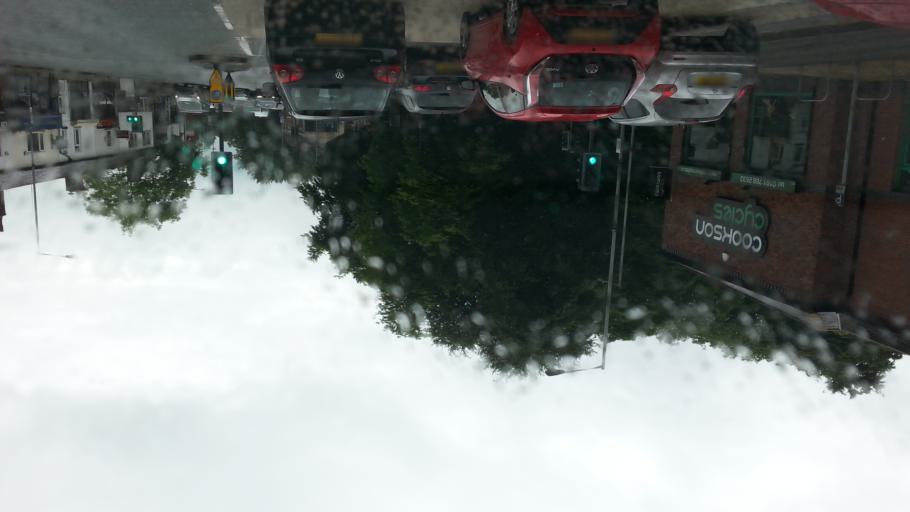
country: GB
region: England
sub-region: Borough of Bury
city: Whitefield
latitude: 53.5475
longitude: -2.2932
